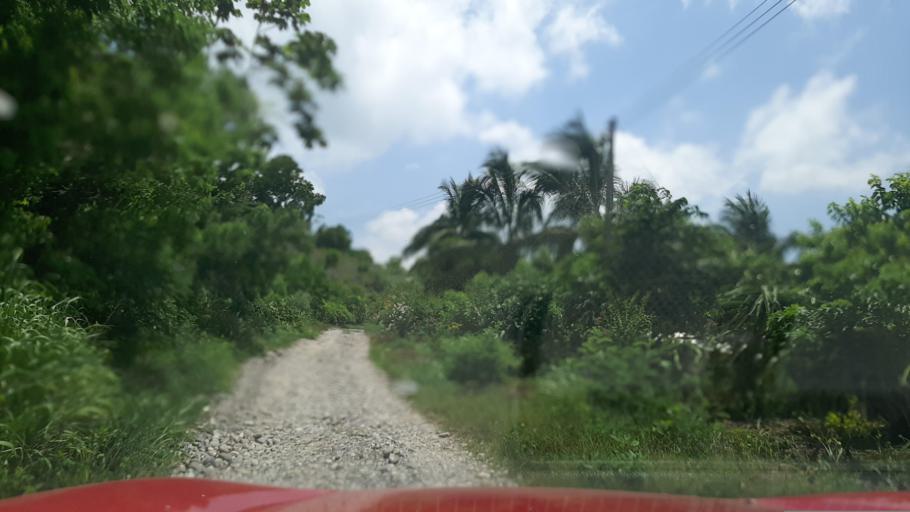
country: MX
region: Veracruz
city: Papantla de Olarte
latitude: 20.4250
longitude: -97.2682
